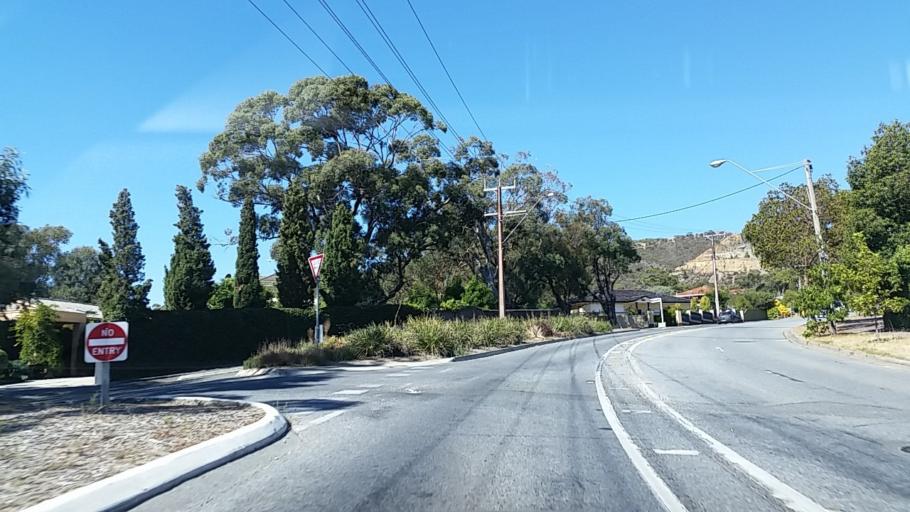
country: AU
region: South Australia
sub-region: Burnside
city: Hazelwood Park
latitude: -34.9378
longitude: 138.6692
